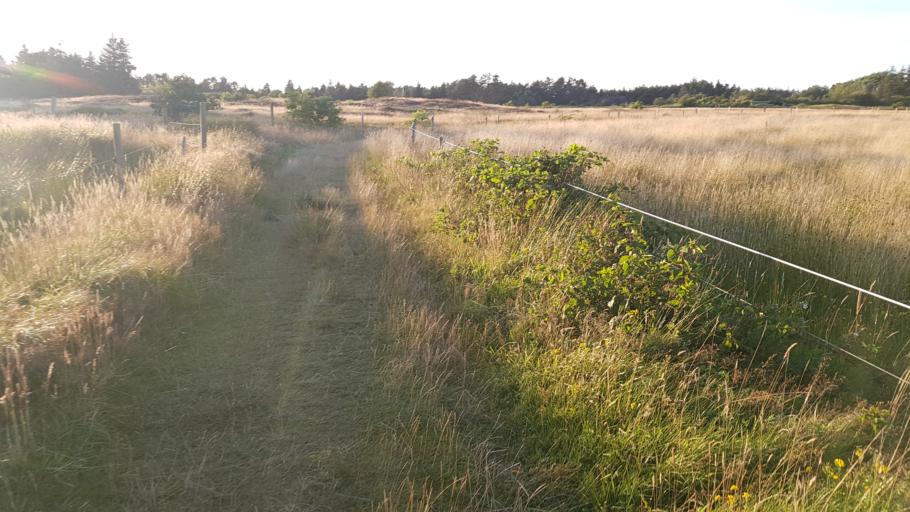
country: DE
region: Schleswig-Holstein
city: List
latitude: 55.1017
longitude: 8.5442
